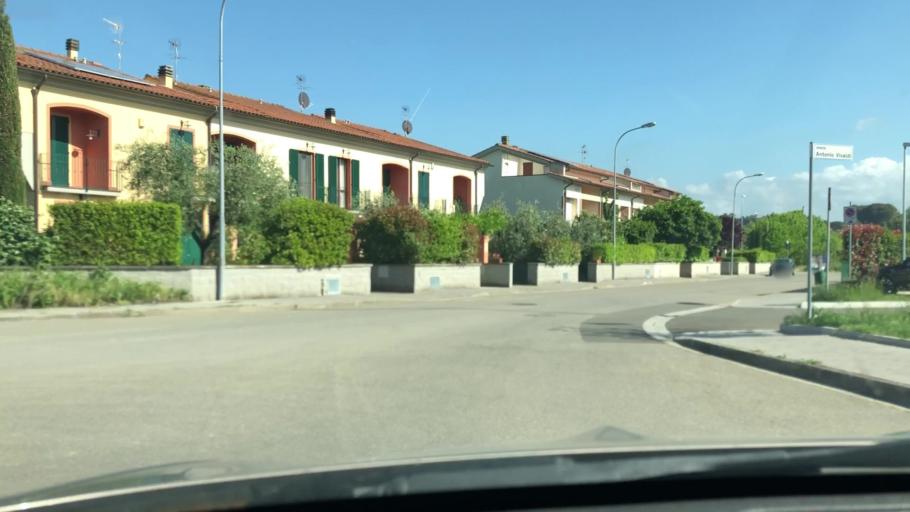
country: IT
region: Tuscany
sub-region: Province of Pisa
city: Capannoli
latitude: 43.5920
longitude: 10.6747
